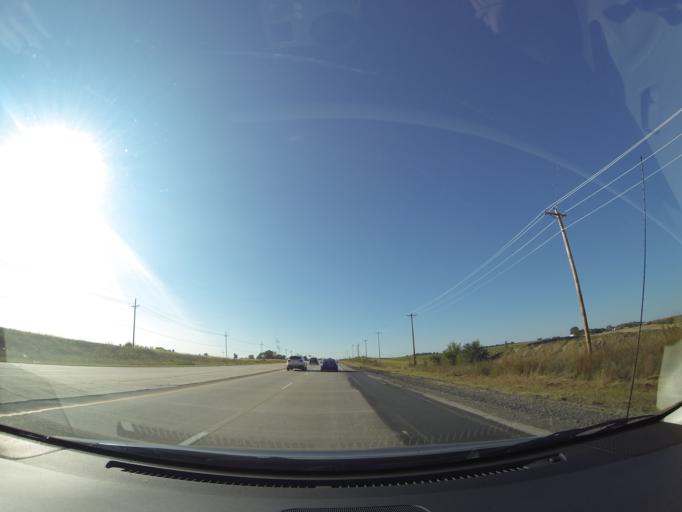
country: US
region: Nebraska
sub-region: Douglas County
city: Elkhorn
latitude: 41.2226
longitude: -96.2345
